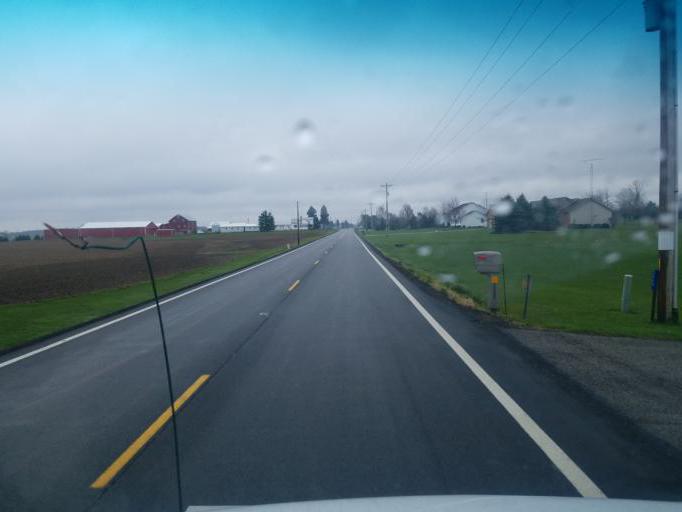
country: US
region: Ohio
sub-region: Huron County
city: Willard
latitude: 40.9604
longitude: -82.8320
